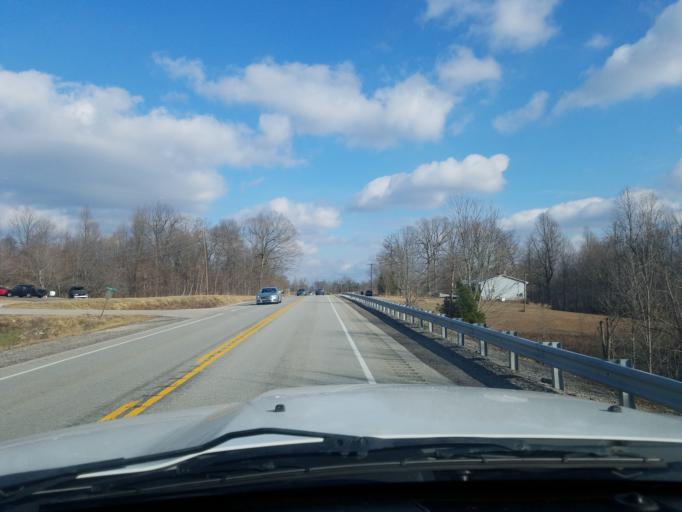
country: US
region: Kentucky
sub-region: Larue County
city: Hodgenville
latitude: 37.4691
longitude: -85.5909
